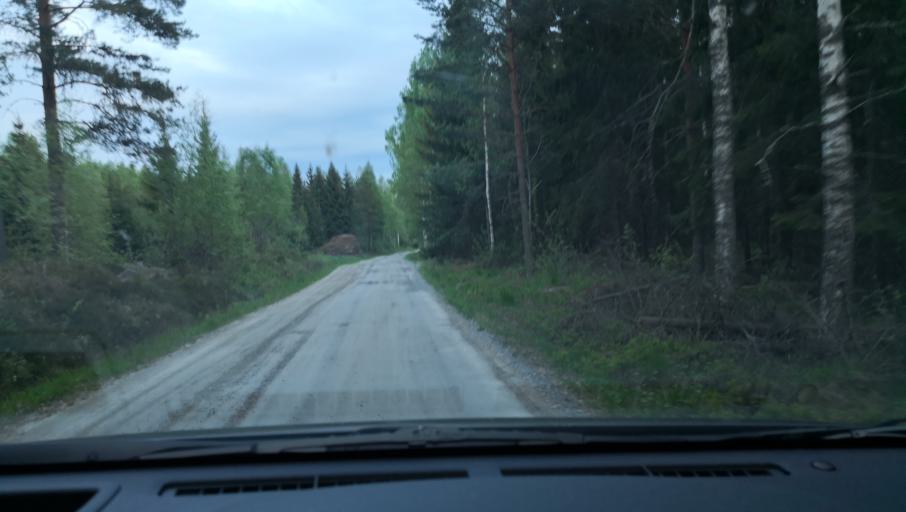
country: SE
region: Vaestmanland
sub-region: Skinnskattebergs Kommun
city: Skinnskatteberg
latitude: 59.7469
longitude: 15.4641
